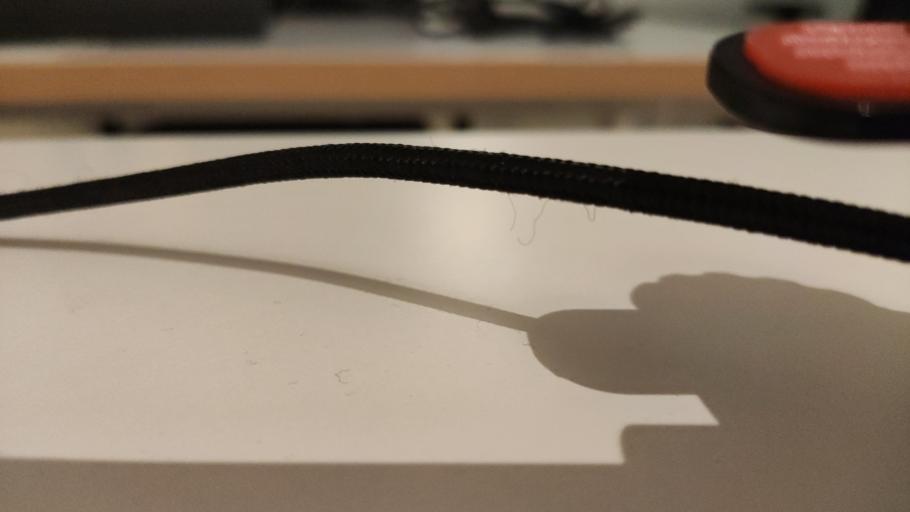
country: RU
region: Moskovskaya
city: Kurovskoye
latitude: 55.5370
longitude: 38.8728
